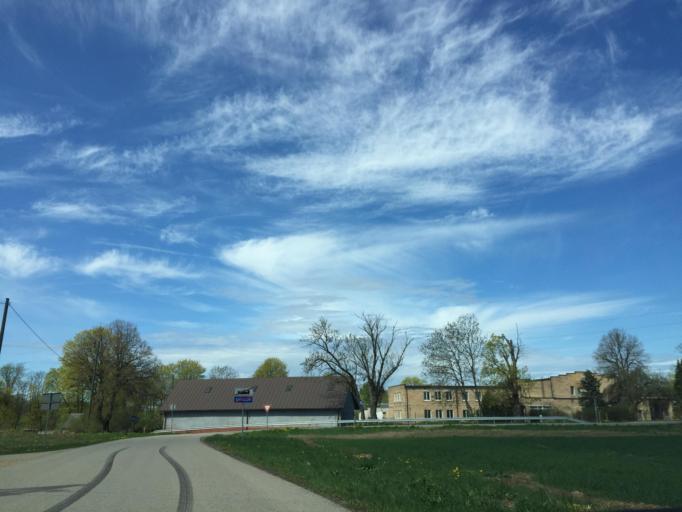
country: LV
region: Sigulda
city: Sigulda
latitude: 57.1320
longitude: 24.8391
